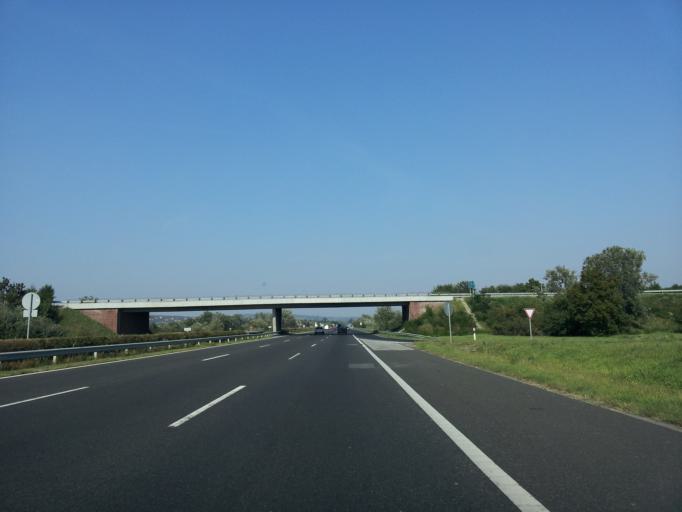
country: HU
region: Fejer
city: Pakozd
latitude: 47.1921
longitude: 18.5077
